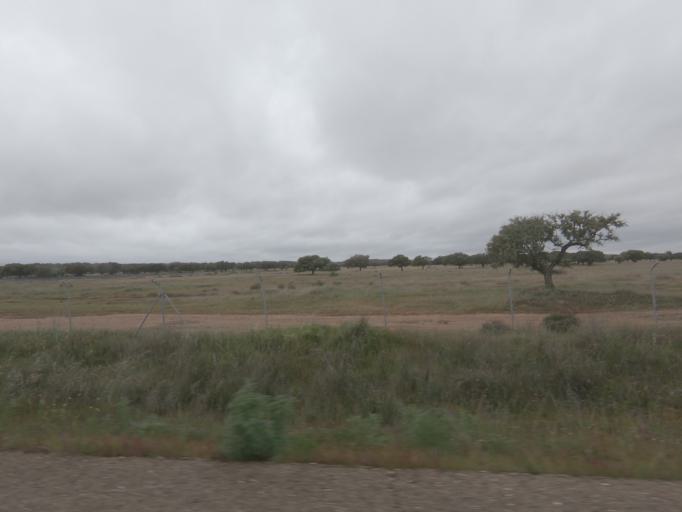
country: ES
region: Extremadura
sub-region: Provincia de Badajoz
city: Villar del Rey
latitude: 39.0127
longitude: -6.8544
